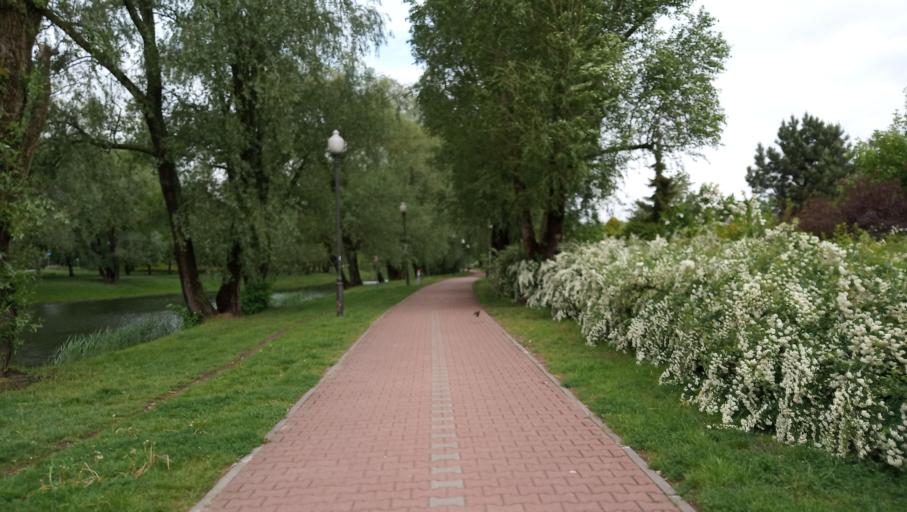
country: PL
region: Masovian Voivodeship
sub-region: Warszawa
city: Zoliborz
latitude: 52.2849
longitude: 20.9802
